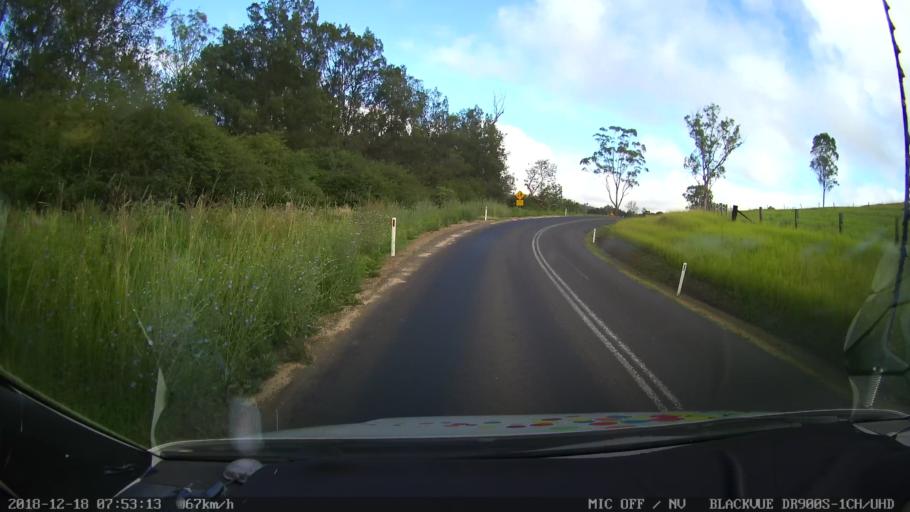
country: AU
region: New South Wales
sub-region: Kyogle
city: Kyogle
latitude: -28.4215
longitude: 152.5827
